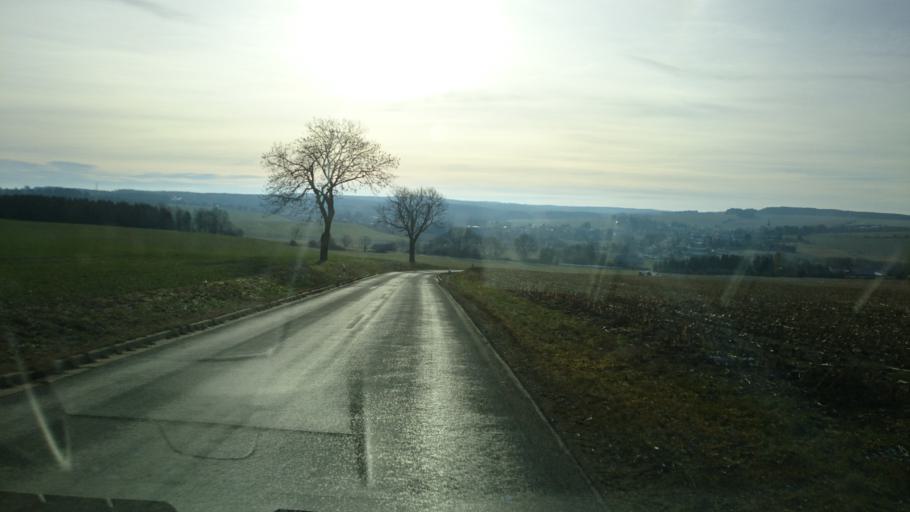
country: DE
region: Thuringia
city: Tanna
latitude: 50.5096
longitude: 11.8665
